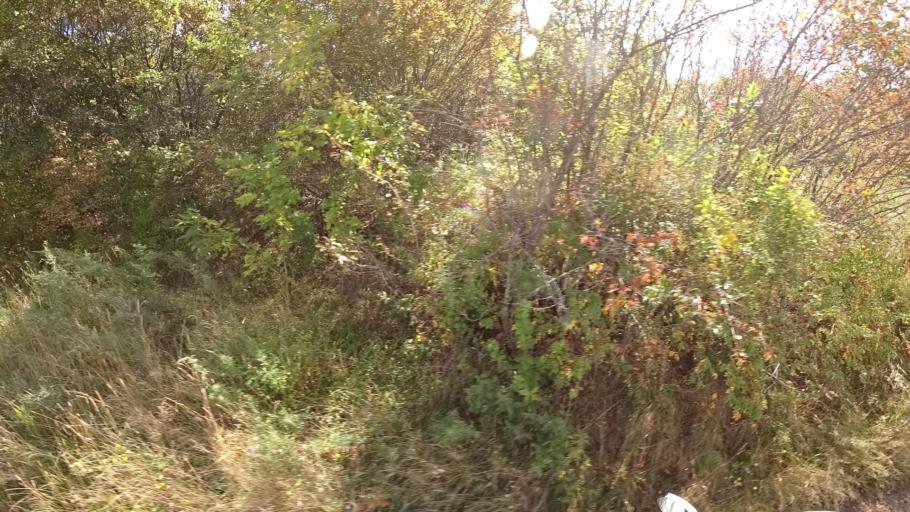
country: RU
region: Primorskiy
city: Kirovskiy
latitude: 44.7597
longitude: 133.6194
